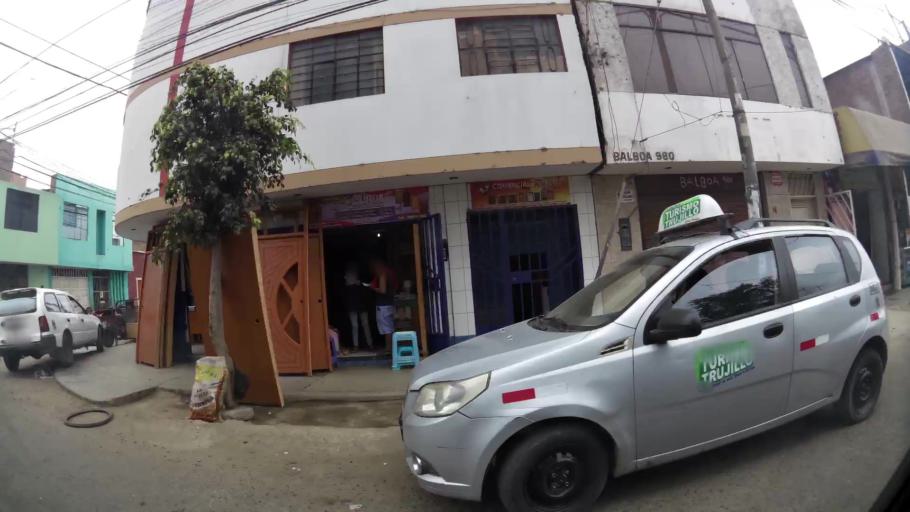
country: PE
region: La Libertad
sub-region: Provincia de Trujillo
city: Trujillo
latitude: -8.1140
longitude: -79.0180
